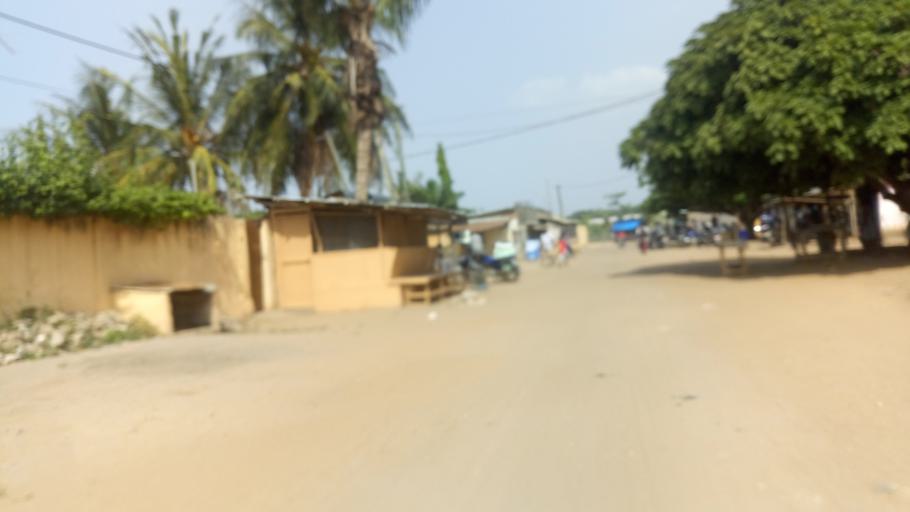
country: TG
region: Maritime
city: Lome
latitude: 6.1690
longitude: 1.2074
